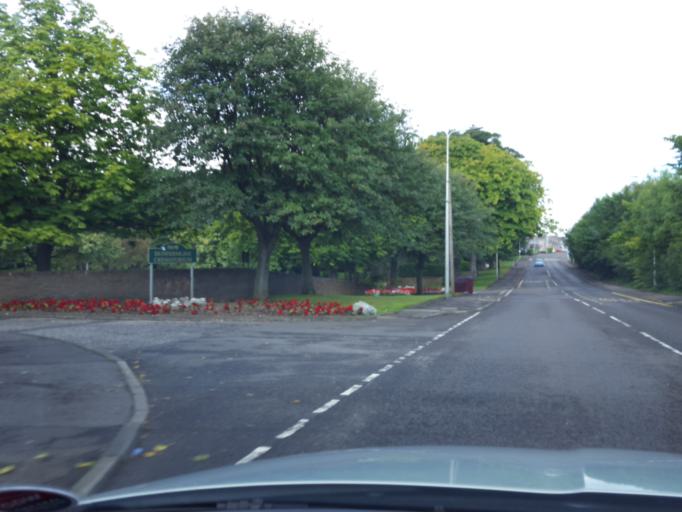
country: GB
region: Scotland
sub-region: Fife
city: Inverkeithing
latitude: 56.0543
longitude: -3.4139
